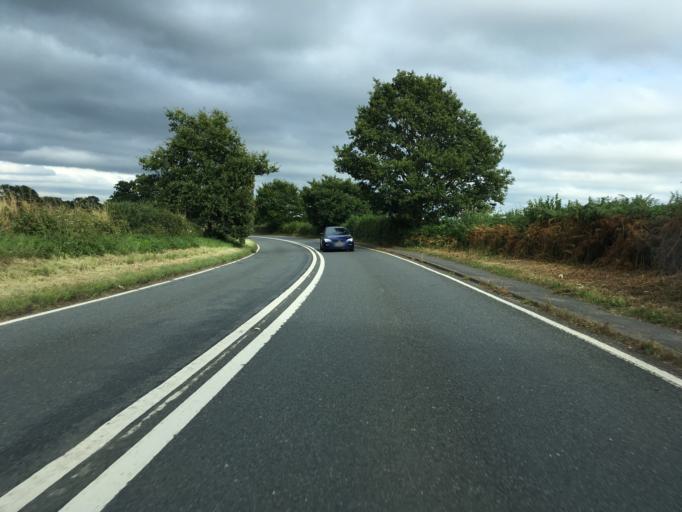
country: GB
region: England
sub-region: Hampshire
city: Petersfield
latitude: 51.0078
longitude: -0.9611
